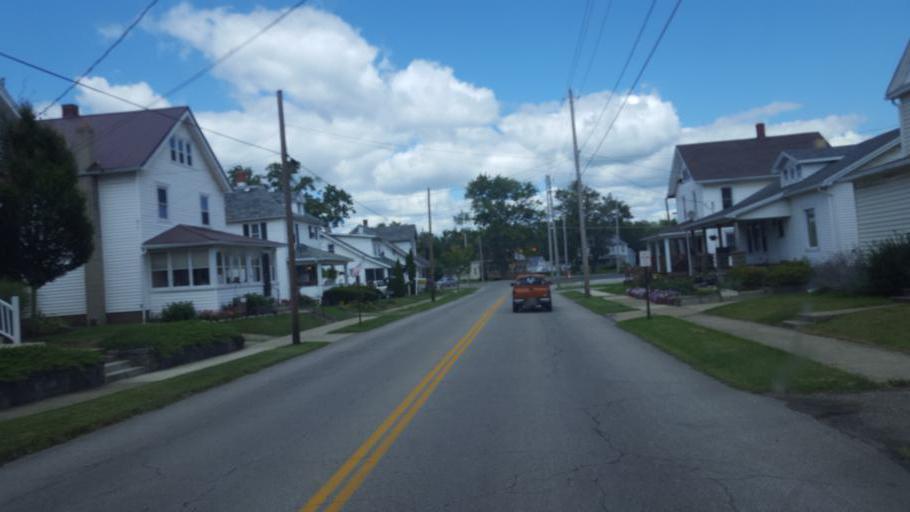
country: US
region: Ohio
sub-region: Ashland County
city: Ashland
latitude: 40.8773
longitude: -82.3128
